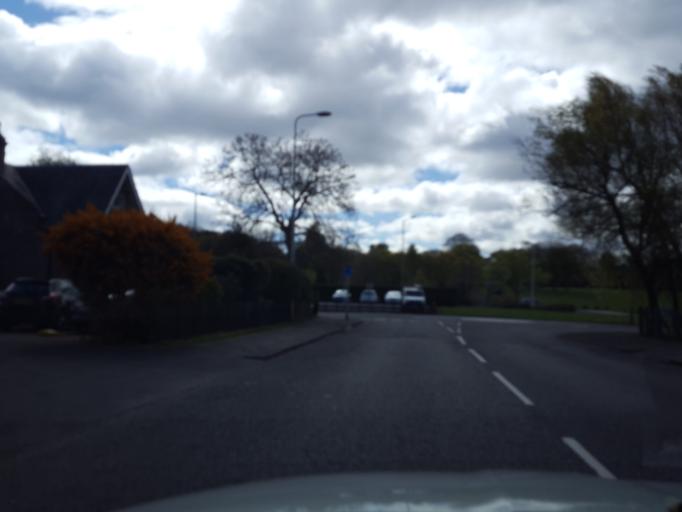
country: GB
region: Scotland
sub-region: Angus
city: Muirhead
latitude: 56.4719
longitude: -3.0495
